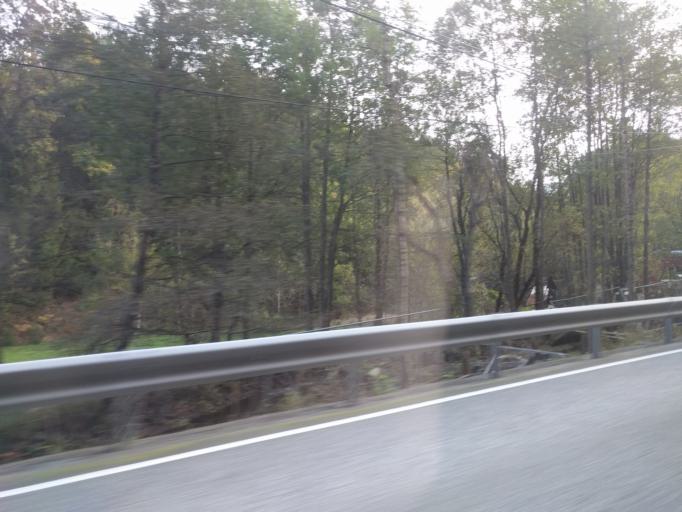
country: NO
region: Vest-Agder
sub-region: Kristiansand
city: Strai
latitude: 58.2408
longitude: 7.8818
